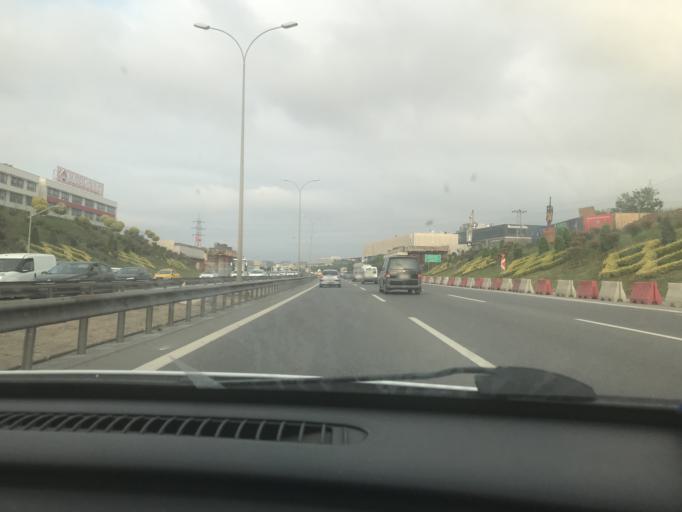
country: TR
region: Istanbul
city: Samandira
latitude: 40.9779
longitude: 29.2245
